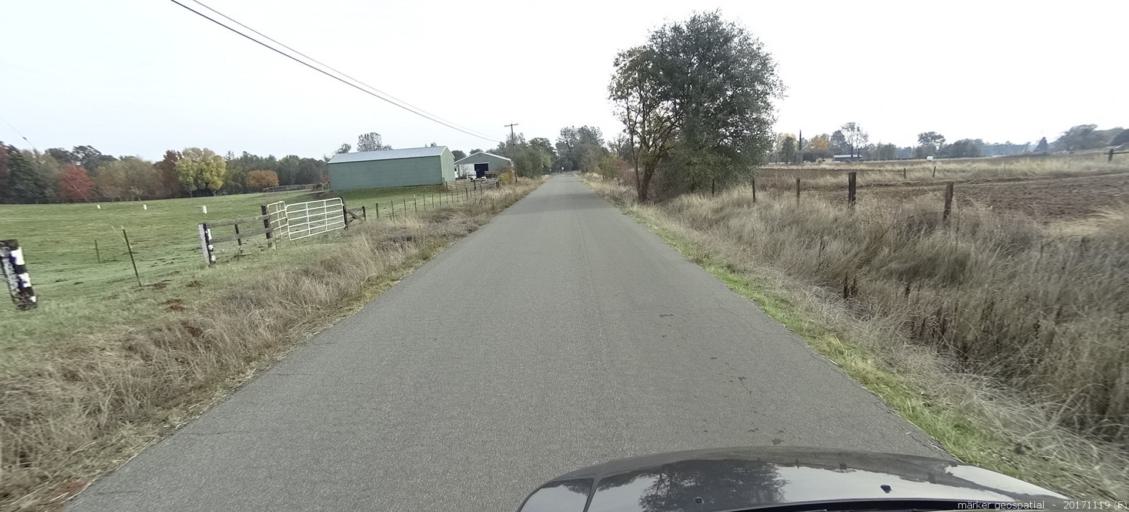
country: US
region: California
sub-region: Shasta County
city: Anderson
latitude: 40.5222
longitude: -122.3368
